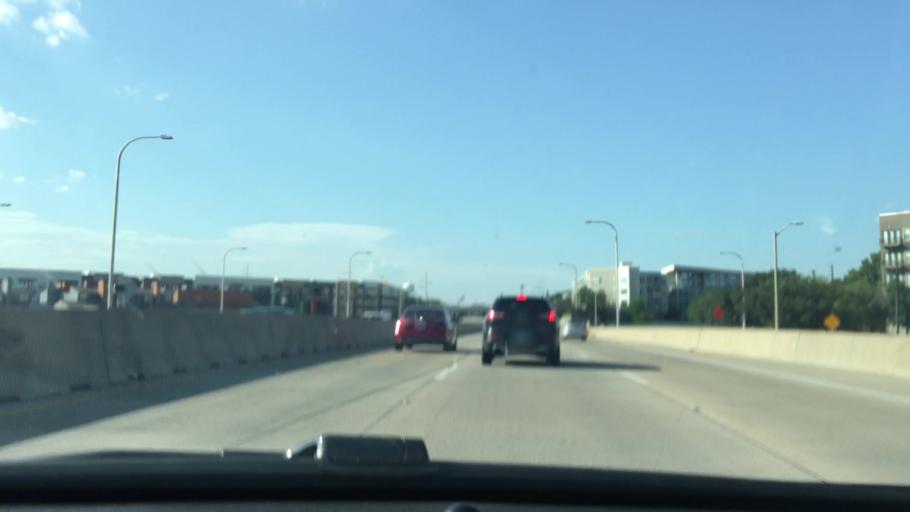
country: US
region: Texas
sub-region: Dallas County
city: Dallas
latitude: 32.8107
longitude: -96.8174
